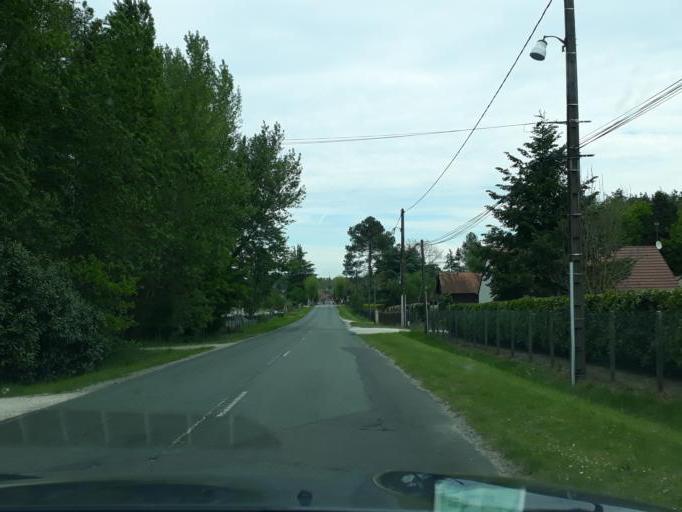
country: FR
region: Centre
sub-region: Departement du Loir-et-Cher
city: Dhuizon
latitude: 47.6497
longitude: 1.6693
